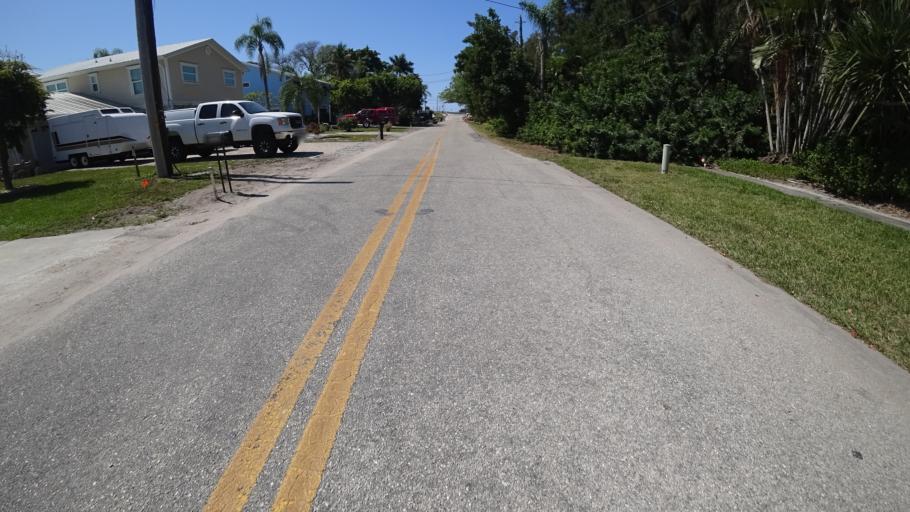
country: US
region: Florida
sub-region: Manatee County
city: Cortez
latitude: 27.4717
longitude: -82.6886
